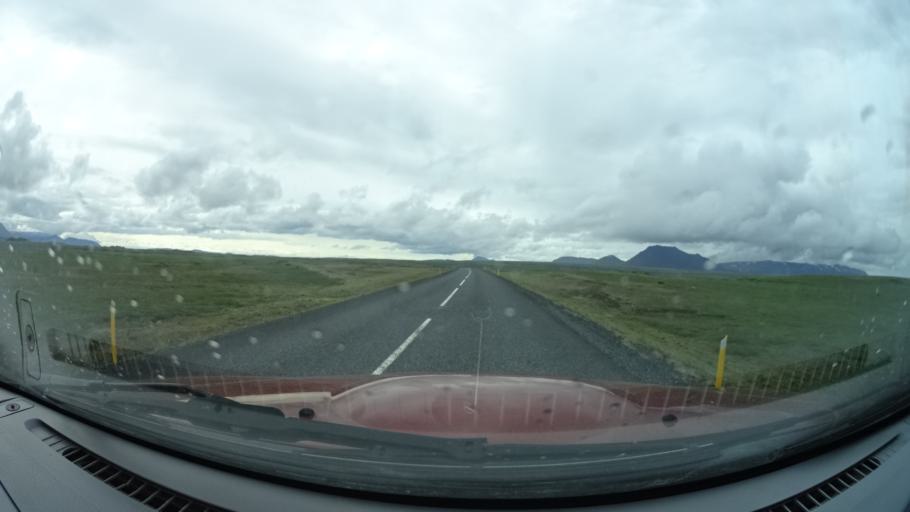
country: IS
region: Northeast
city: Laugar
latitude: 65.6603
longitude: -16.5323
